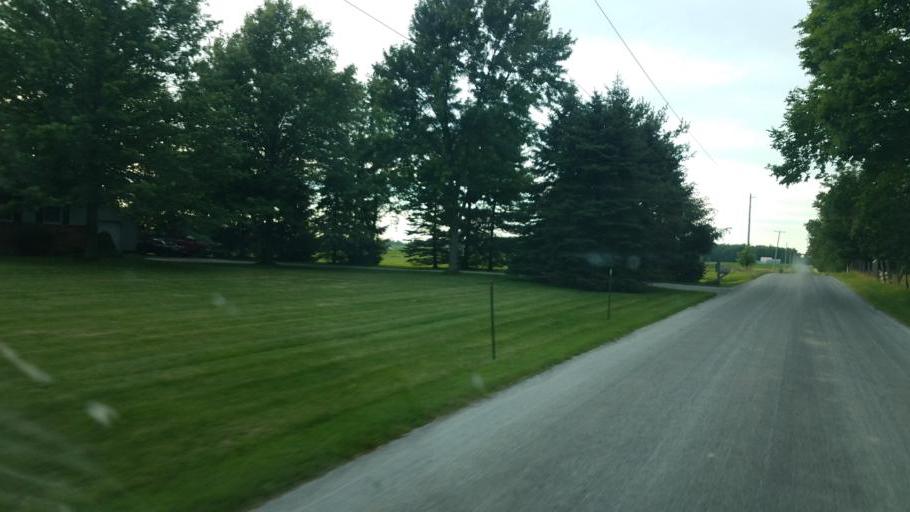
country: US
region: Ohio
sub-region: Huron County
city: Greenwich
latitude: 40.9124
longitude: -82.4744
